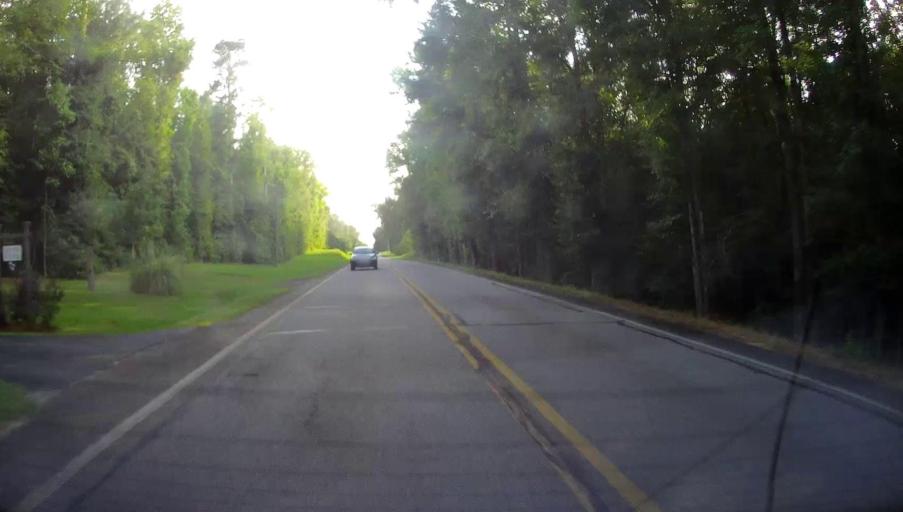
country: US
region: Georgia
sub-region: Crawford County
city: Knoxville
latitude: 32.8617
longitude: -83.9966
